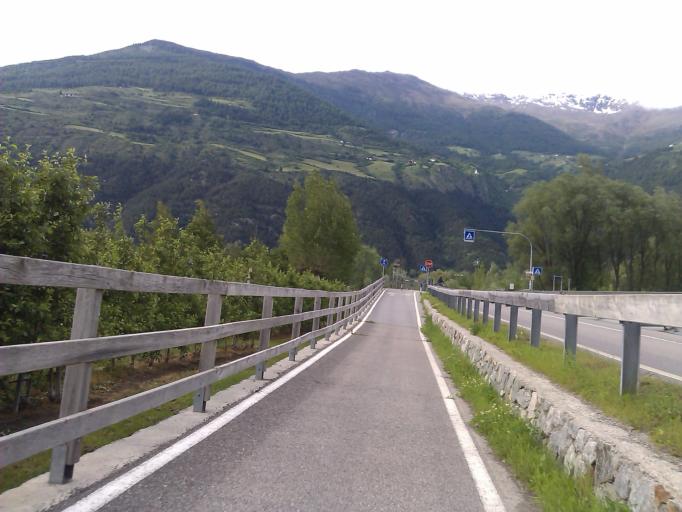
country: IT
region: Trentino-Alto Adige
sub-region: Bolzano
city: Lasa
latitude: 46.6215
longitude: 10.6479
